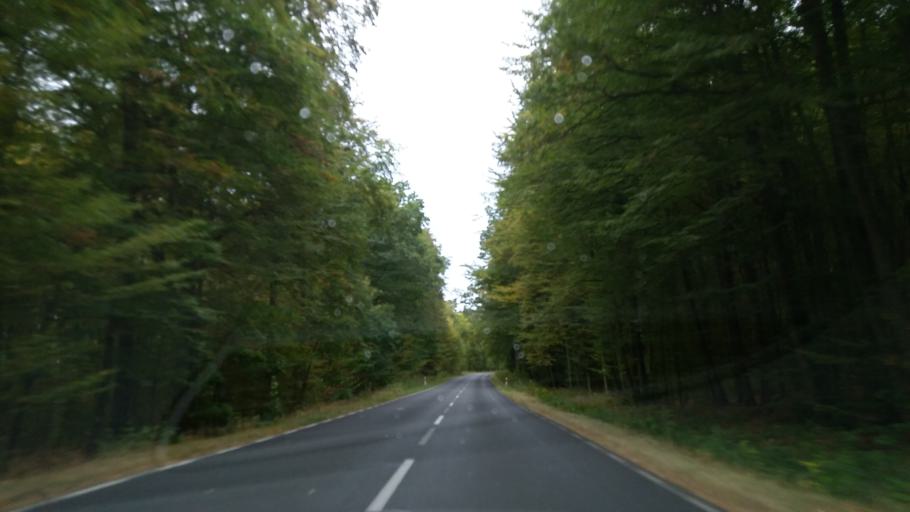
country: PL
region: West Pomeranian Voivodeship
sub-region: Powiat mysliborski
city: Barlinek
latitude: 52.8976
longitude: 15.1930
